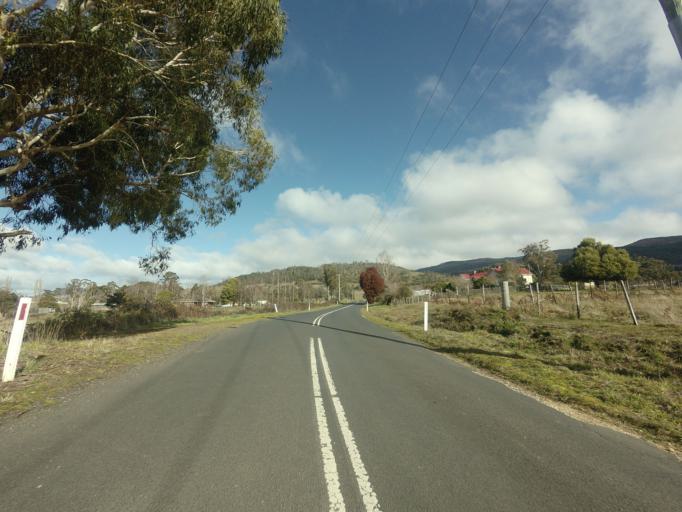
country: AU
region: Tasmania
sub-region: Derwent Valley
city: New Norfolk
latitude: -42.6014
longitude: 146.7067
